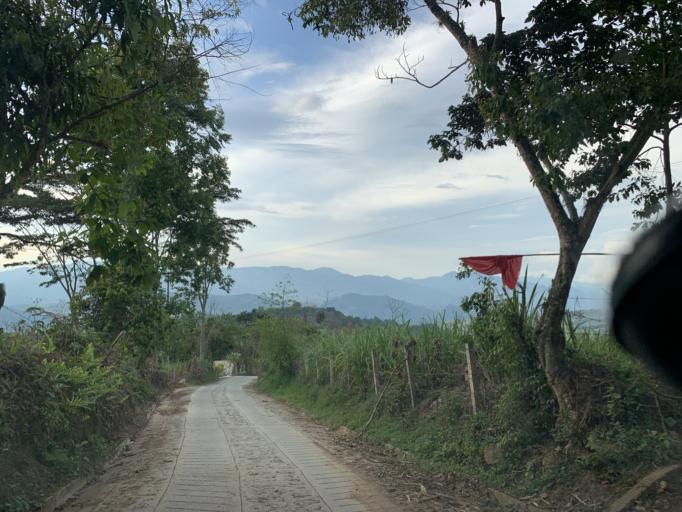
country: CO
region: Boyaca
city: Santana
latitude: 6.0678
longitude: -73.4838
